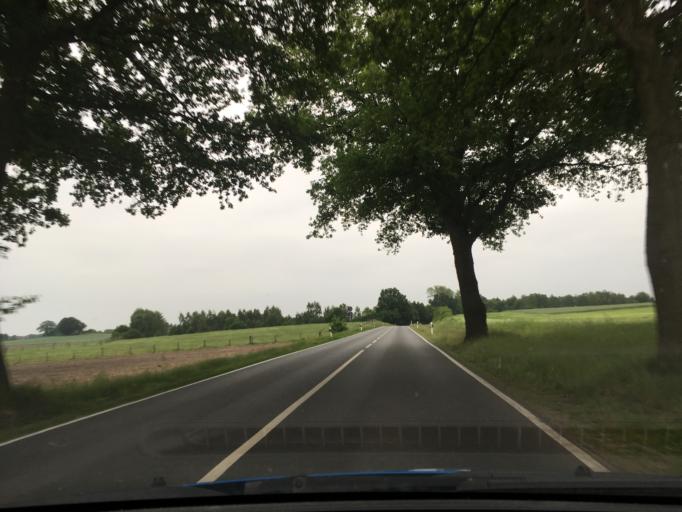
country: DE
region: Lower Saxony
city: Wulfsen
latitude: 53.3402
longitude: 10.1482
